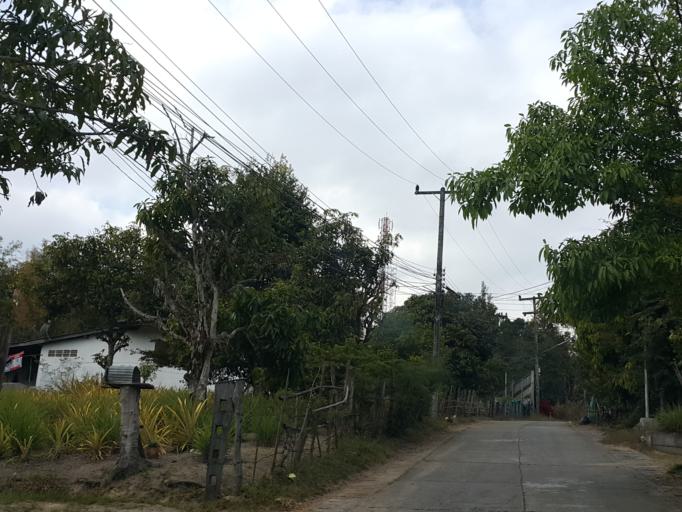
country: TH
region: Chiang Mai
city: Om Koi
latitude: 17.7980
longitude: 98.3551
